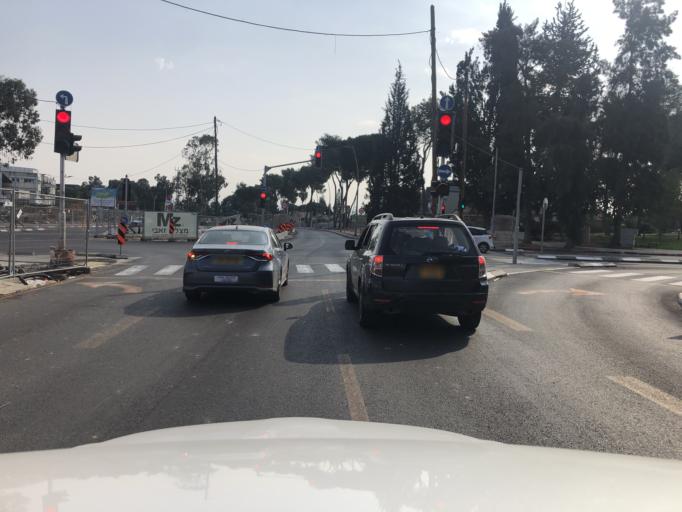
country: IL
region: Central District
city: Kfar Saba
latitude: 32.1714
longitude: 34.9238
